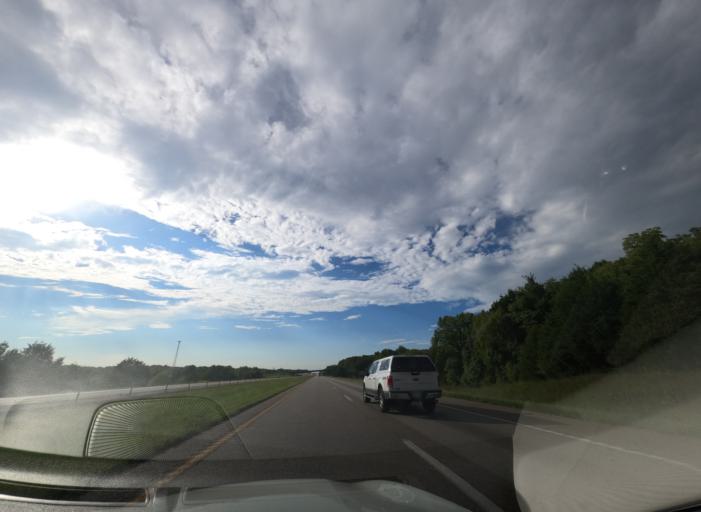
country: US
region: Missouri
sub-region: Sainte Genevieve County
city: Sainte Genevieve
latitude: 38.0240
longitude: -90.2382
